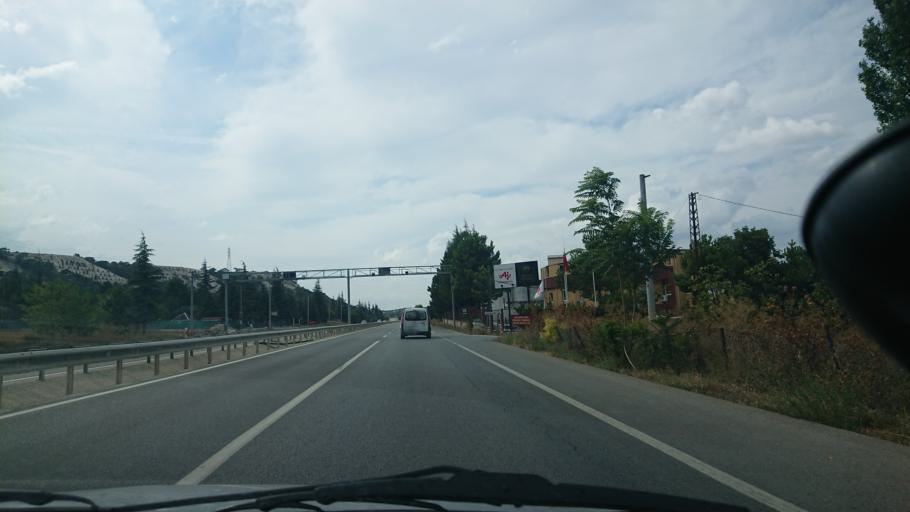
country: TR
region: Eskisehir
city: Eskisehir
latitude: 39.7271
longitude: 30.3611
